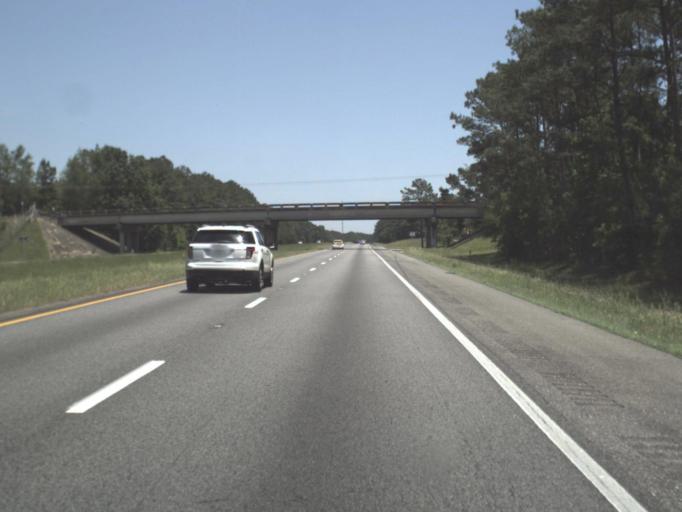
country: US
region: Florida
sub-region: Jefferson County
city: Monticello
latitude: 30.4783
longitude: -83.9226
